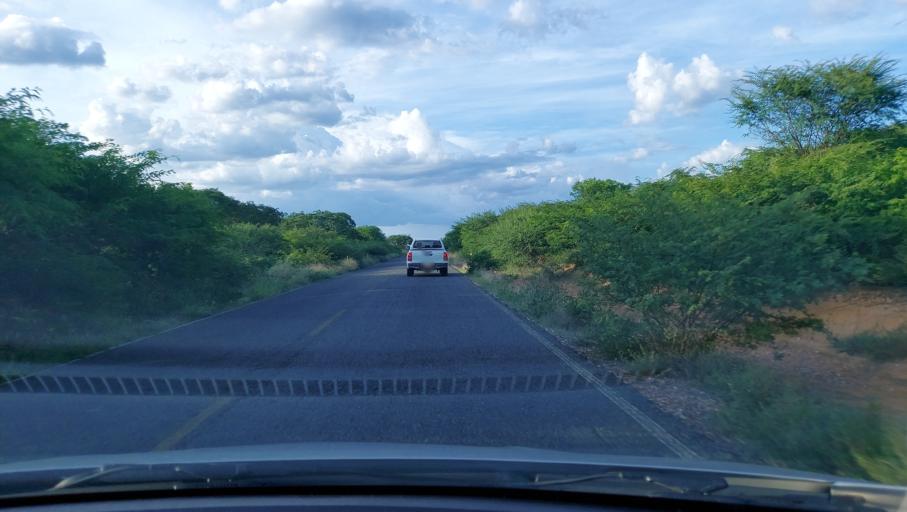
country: BR
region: Bahia
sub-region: Oliveira Dos Brejinhos
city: Beira Rio
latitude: -12.1891
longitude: -42.5386
